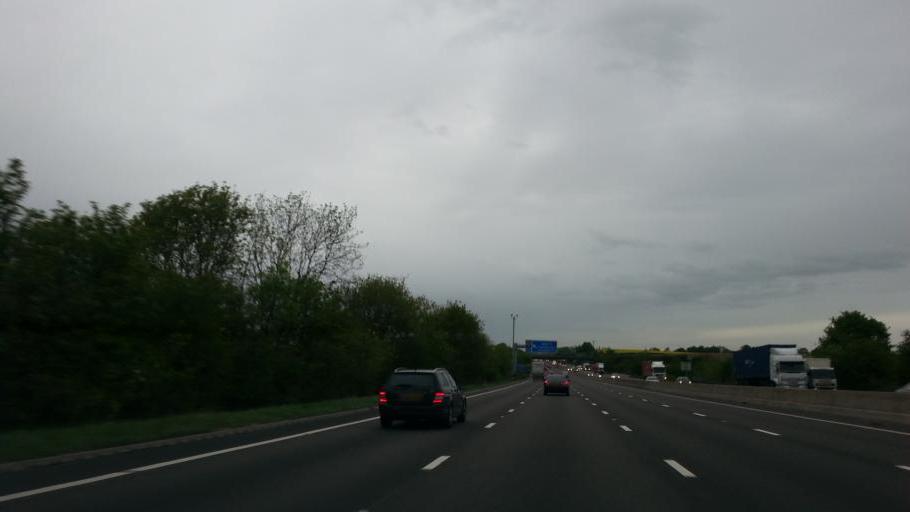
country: GB
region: England
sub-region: Rotherham
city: Wales
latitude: 53.3473
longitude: -1.2889
